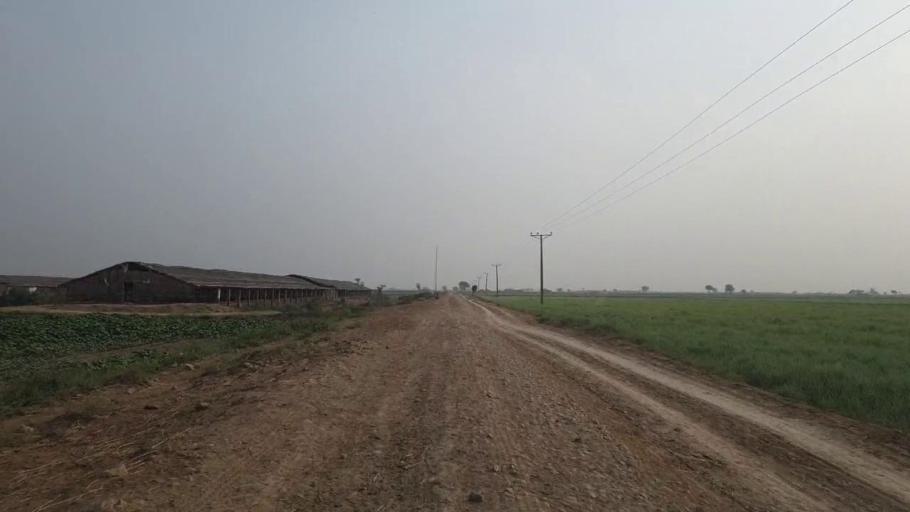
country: PK
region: Sindh
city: Mirpur Batoro
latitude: 24.5521
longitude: 68.4207
